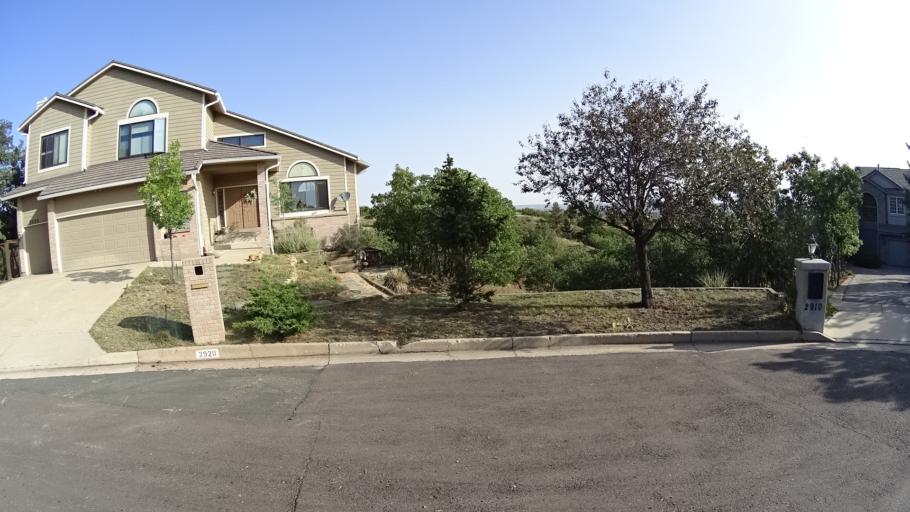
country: US
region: Colorado
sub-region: El Paso County
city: Colorado Springs
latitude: 38.8242
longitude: -104.8724
